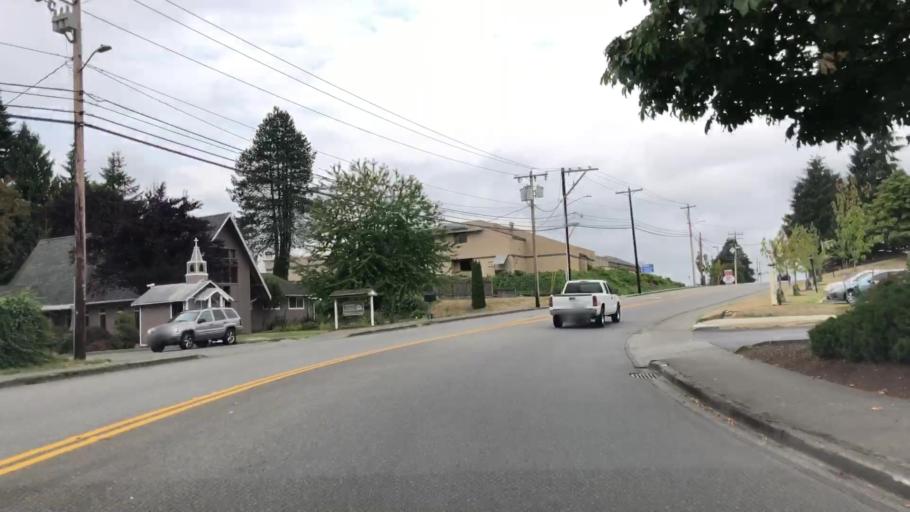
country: US
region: Washington
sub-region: Snohomish County
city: Snohomish
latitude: 47.9273
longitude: -122.0935
